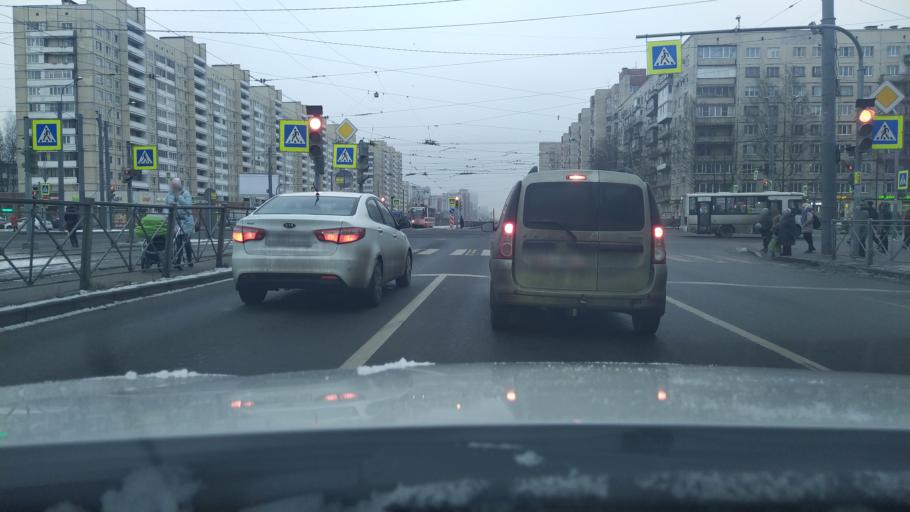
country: RU
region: St.-Petersburg
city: Grazhdanka
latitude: 60.0397
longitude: 30.3999
